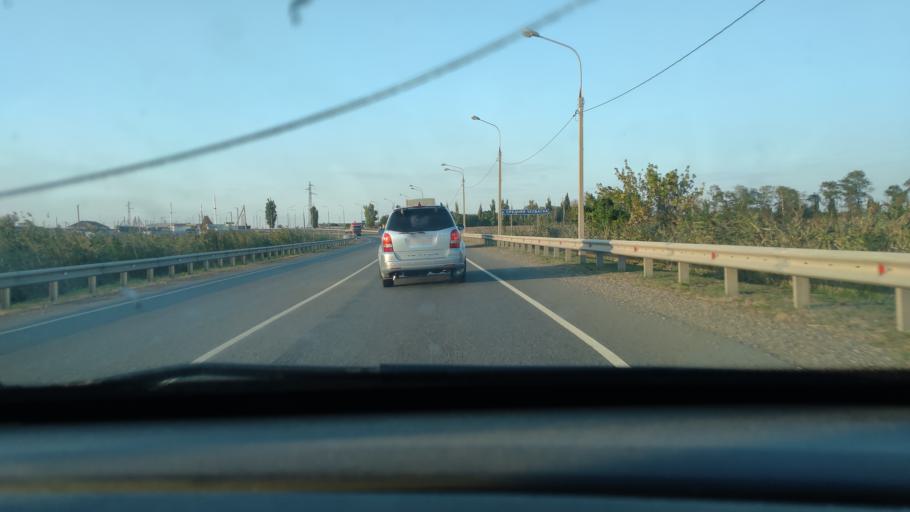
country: RU
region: Krasnodarskiy
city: Kanevskaya
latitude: 46.0720
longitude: 39.0139
